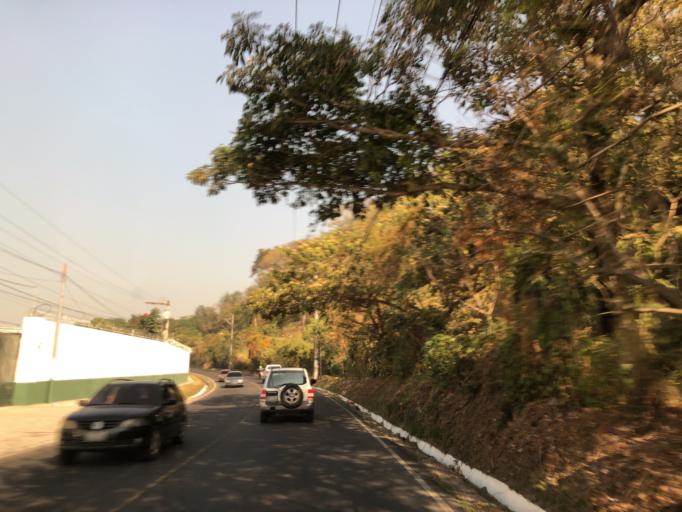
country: GT
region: Guatemala
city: Villa Canales
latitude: 14.4904
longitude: -90.5359
